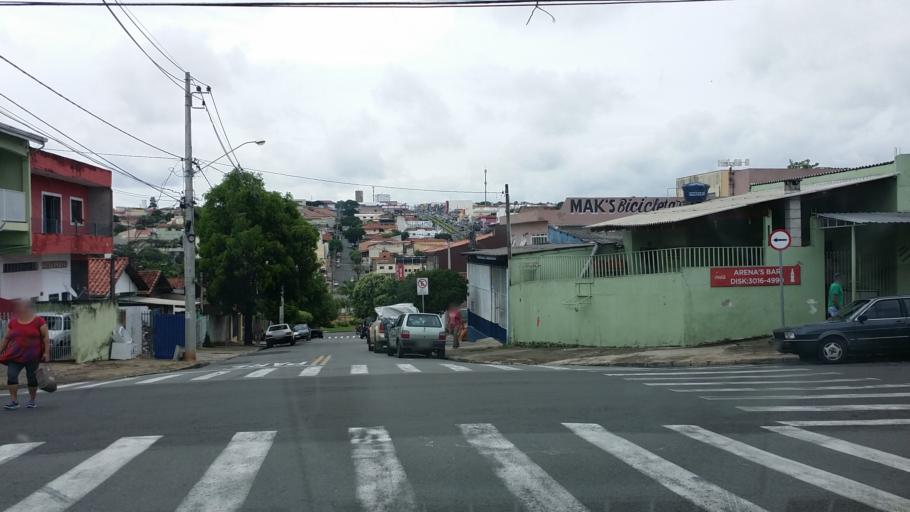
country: BR
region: Sao Paulo
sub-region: Indaiatuba
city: Indaiatuba
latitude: -23.1190
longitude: -47.2307
